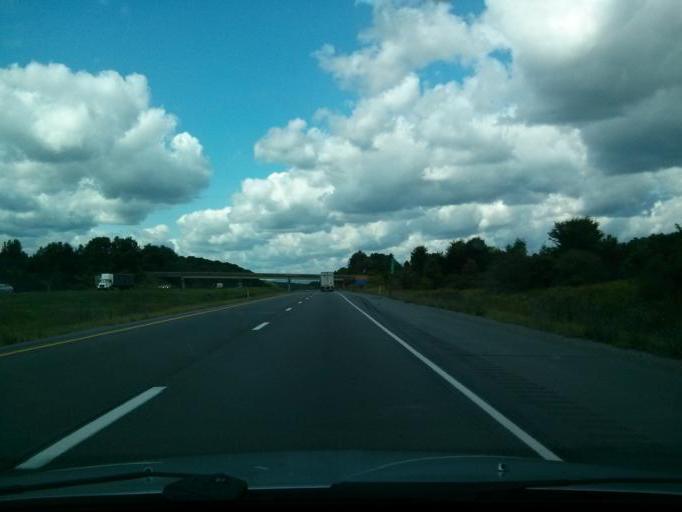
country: US
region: Pennsylvania
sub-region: Clearfield County
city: Treasure Lake
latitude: 41.1214
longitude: -78.6496
